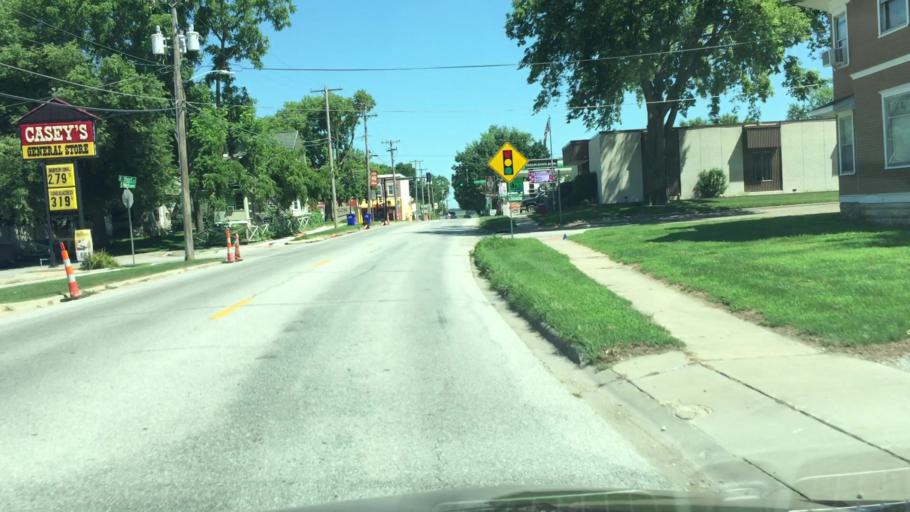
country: US
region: Iowa
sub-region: Johnson County
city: Solon
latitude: 41.8059
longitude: -91.4929
